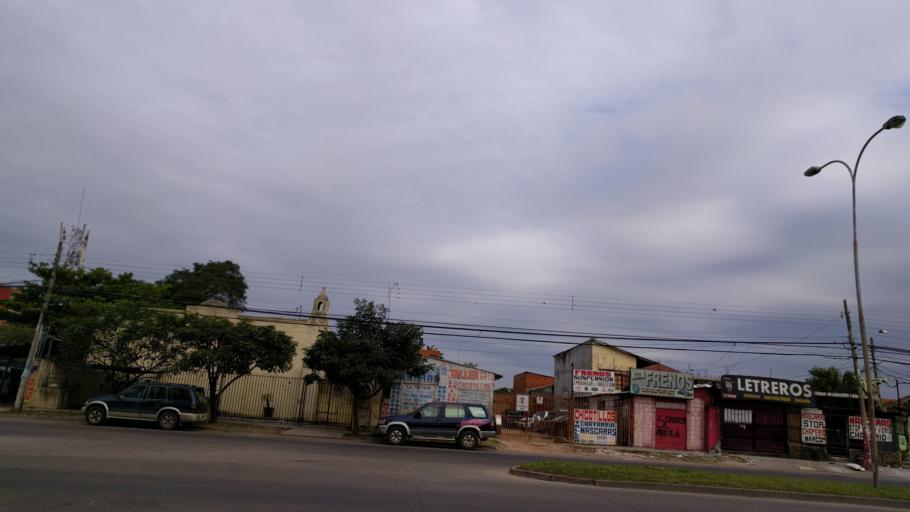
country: BO
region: Santa Cruz
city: Santa Cruz de la Sierra
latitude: -17.7735
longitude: -63.1640
